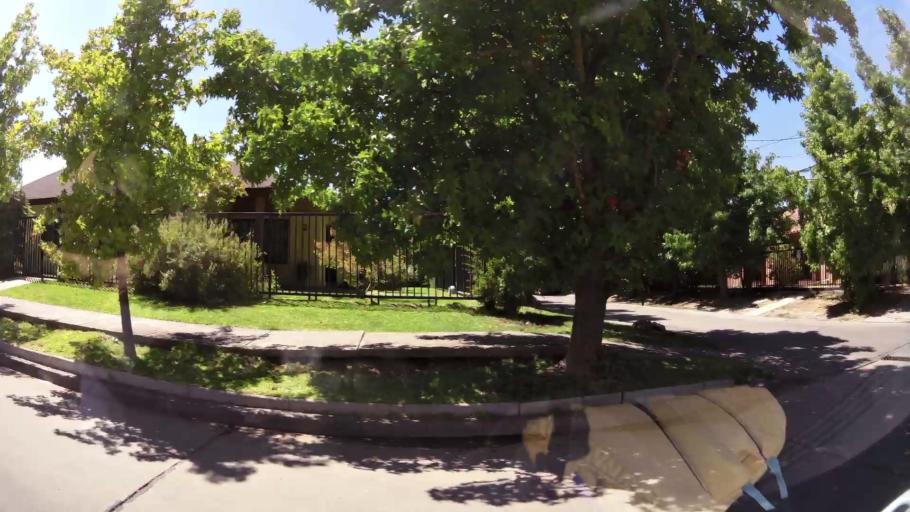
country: CL
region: Maule
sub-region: Provincia de Curico
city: Curico
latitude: -34.9806
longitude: -71.2217
